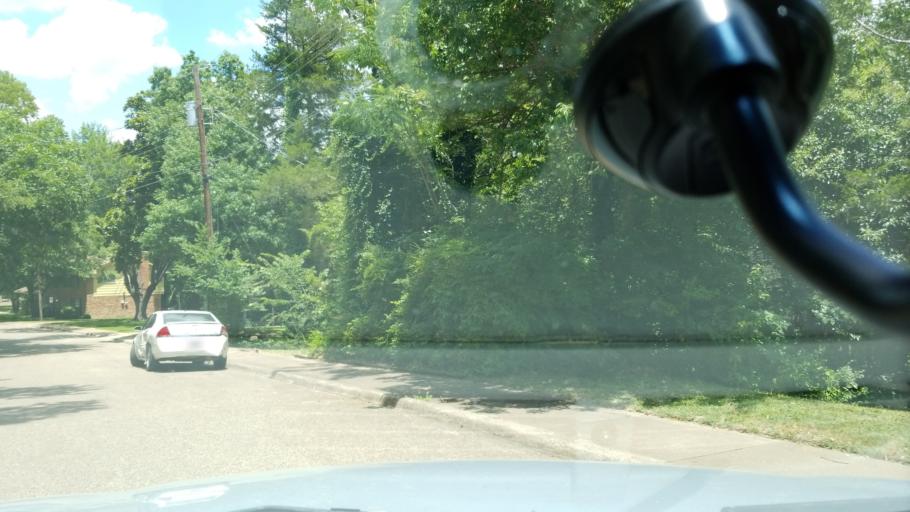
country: US
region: Texas
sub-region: Dallas County
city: Cockrell Hill
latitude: 32.7031
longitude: -96.8804
